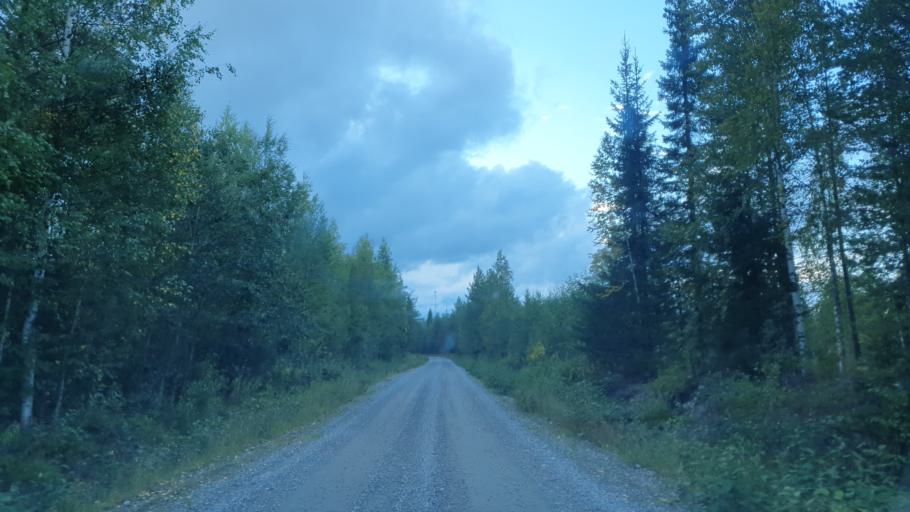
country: FI
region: Kainuu
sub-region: Kehys-Kainuu
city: Kuhmo
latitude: 64.3372
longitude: 29.8977
